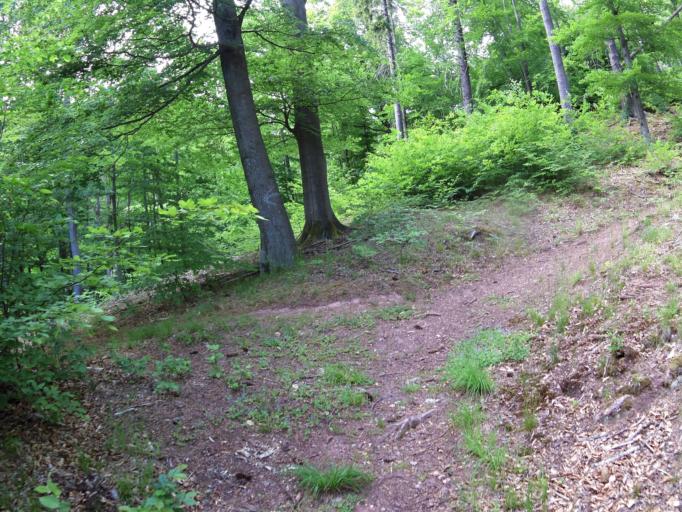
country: DE
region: Thuringia
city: Wolfsburg-Unkeroda
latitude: 50.9221
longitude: 10.2986
